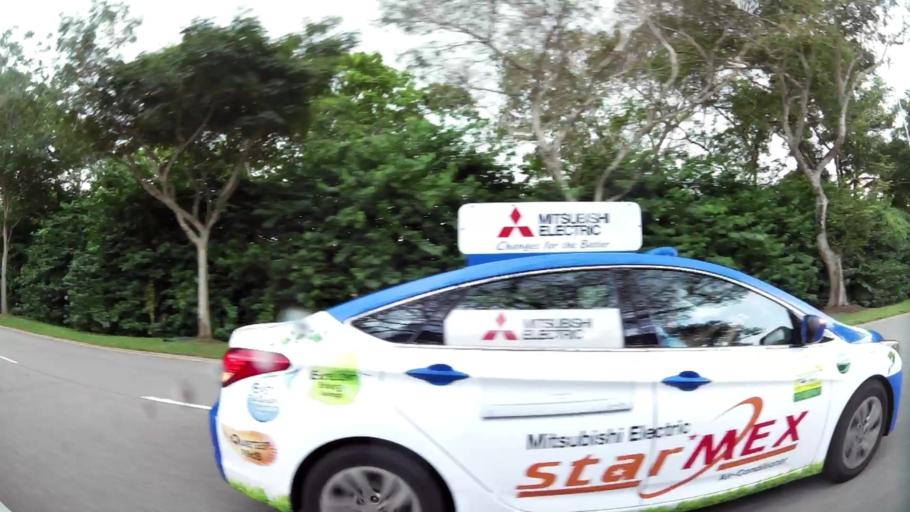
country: SG
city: Singapore
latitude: 1.3259
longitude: 103.9693
